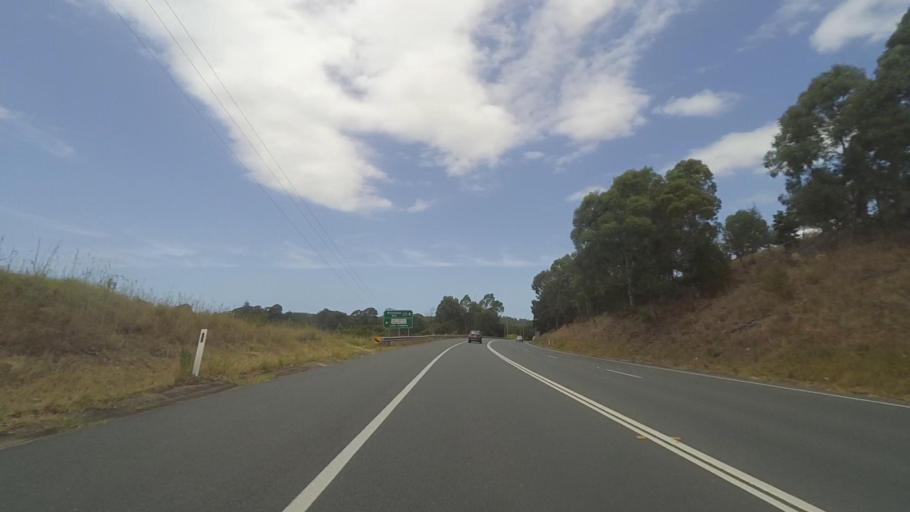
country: AU
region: New South Wales
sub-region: Shoalhaven Shire
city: Milton
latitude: -35.2570
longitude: 150.4265
